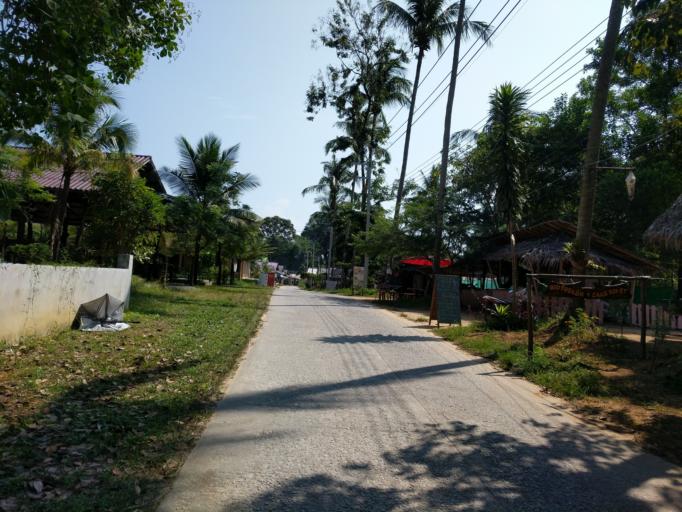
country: TH
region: Ranong
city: Kapoe
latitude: 9.7403
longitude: 98.4175
